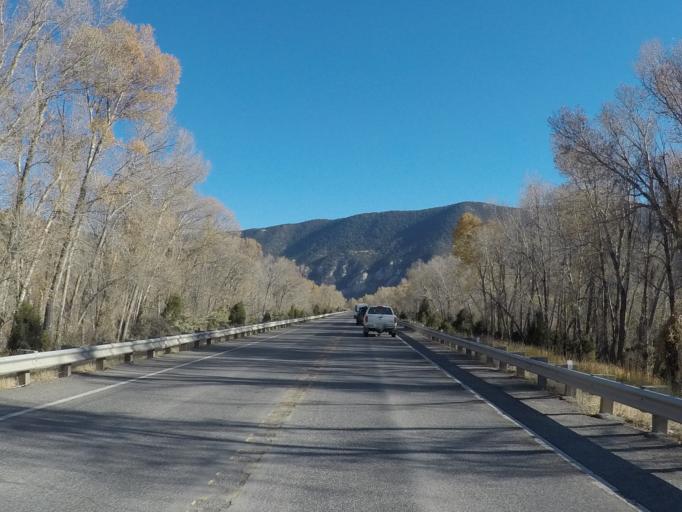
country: US
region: Montana
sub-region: Park County
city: Livingston
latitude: 45.5791
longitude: -110.5817
